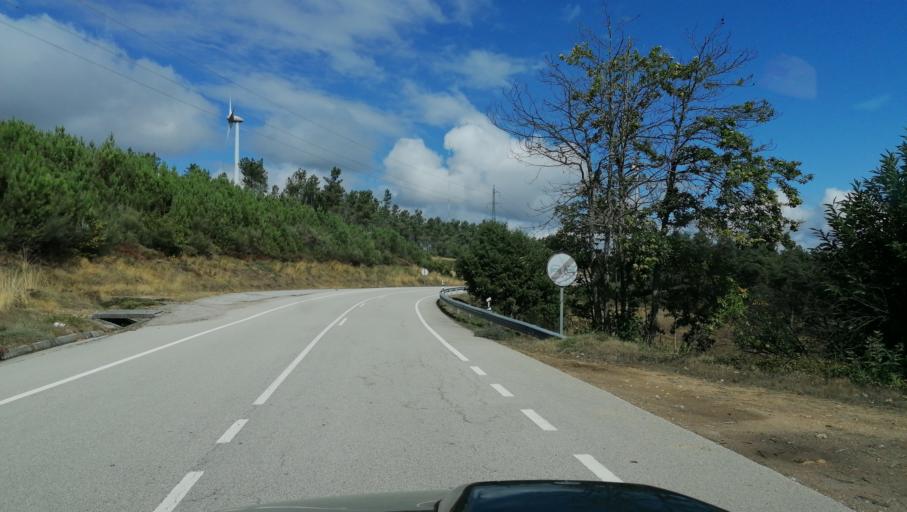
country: PT
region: Vila Real
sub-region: Vila Pouca de Aguiar
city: Vila Pouca de Aguiar
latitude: 41.5206
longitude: -7.5941
